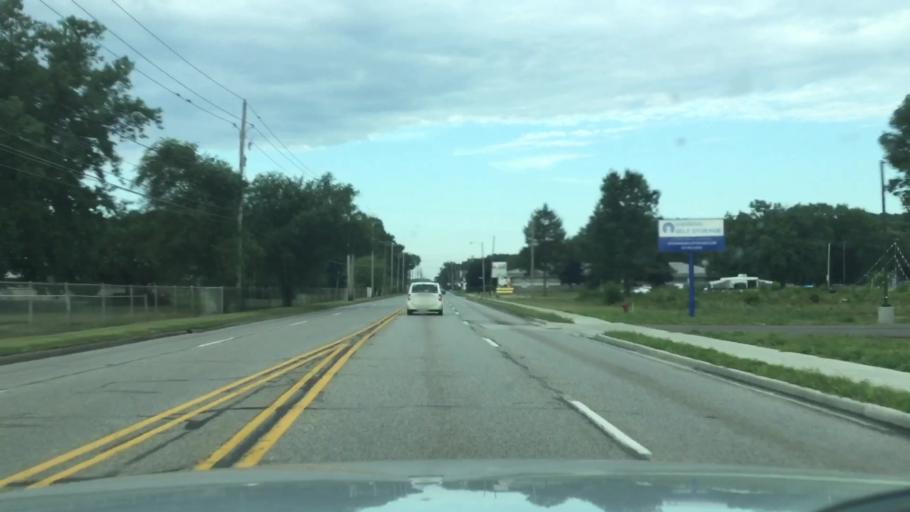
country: US
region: Michigan
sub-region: Muskegon County
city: Roosevelt Park
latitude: 43.2054
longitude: -86.2687
